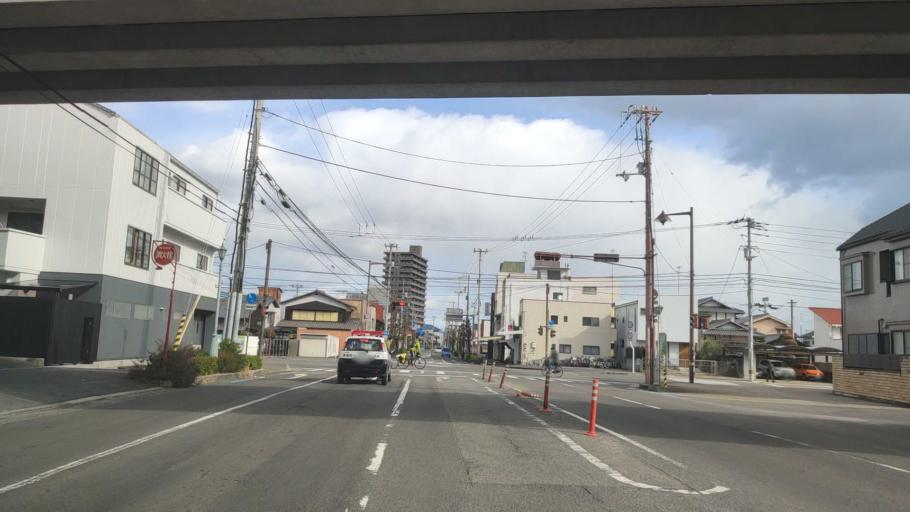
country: JP
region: Ehime
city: Hojo
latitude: 34.0668
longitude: 132.9912
